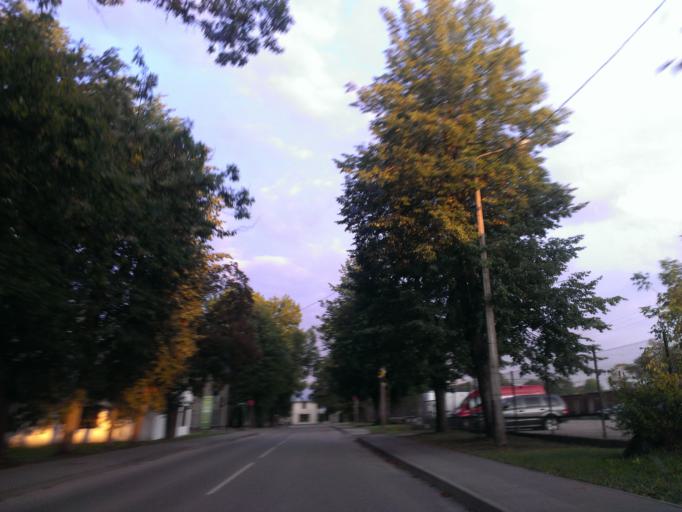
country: LV
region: Ogre
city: Ogre
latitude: 56.8166
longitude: 24.6018
